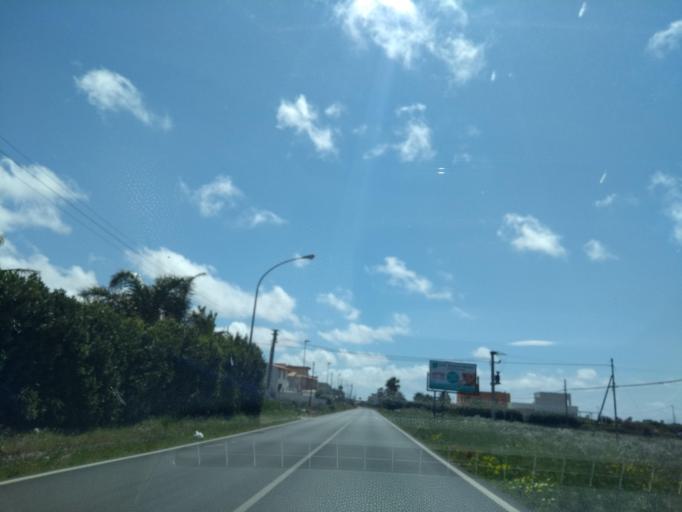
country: IT
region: Sicily
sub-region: Trapani
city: Marsala
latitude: 37.8700
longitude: 12.5184
